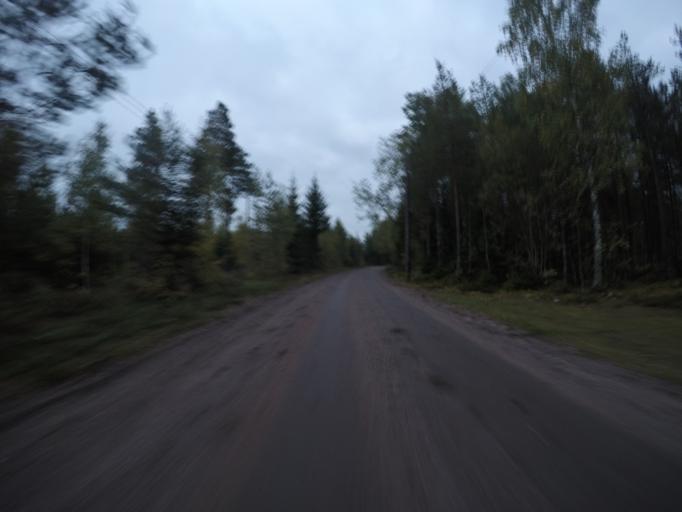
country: SE
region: Vaestmanland
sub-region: Kungsors Kommun
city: Kungsoer
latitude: 59.3806
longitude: 16.1153
